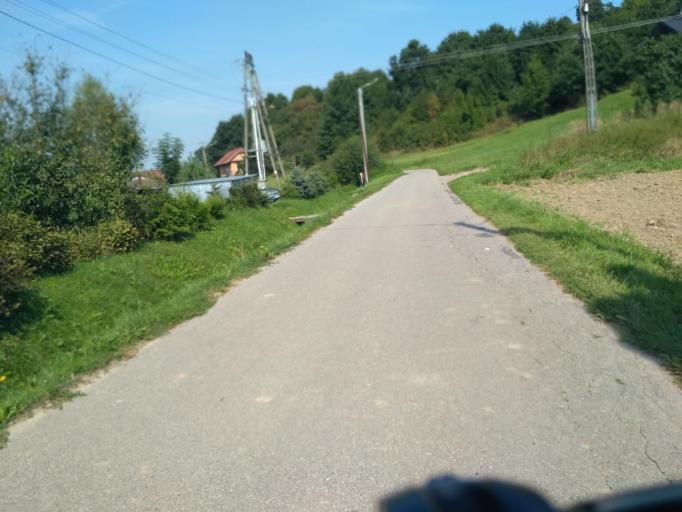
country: PL
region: Subcarpathian Voivodeship
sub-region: Powiat strzyzowski
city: Jawornik
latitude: 49.8209
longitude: 21.8425
